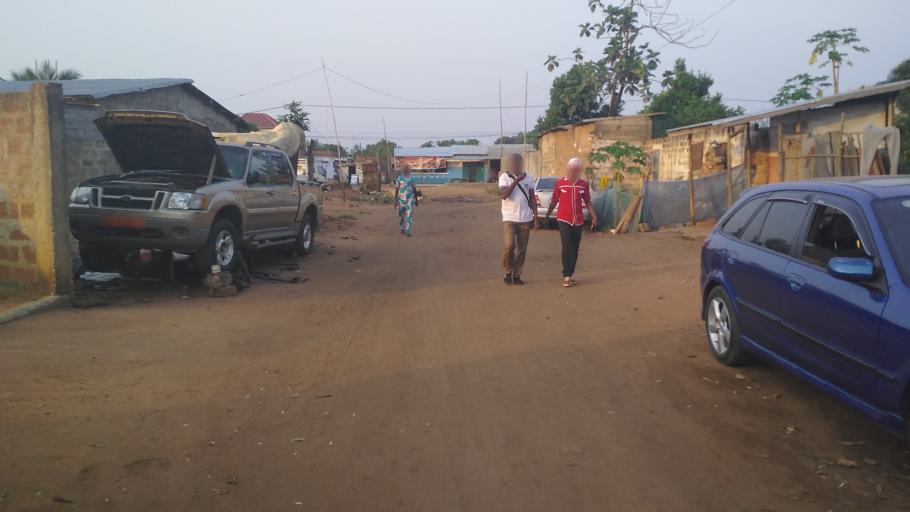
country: BJ
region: Atlantique
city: Abomey-Calavi
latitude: 6.4093
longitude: 2.3401
